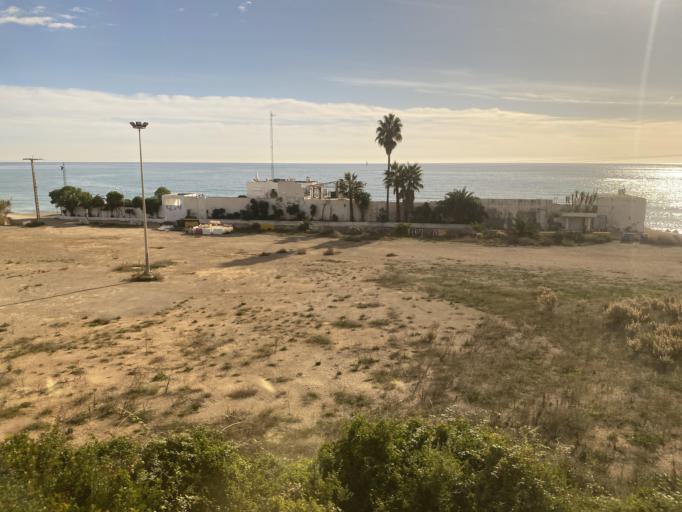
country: ES
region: Catalonia
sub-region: Provincia de Barcelona
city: Sitges
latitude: 41.2240
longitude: 1.7750
